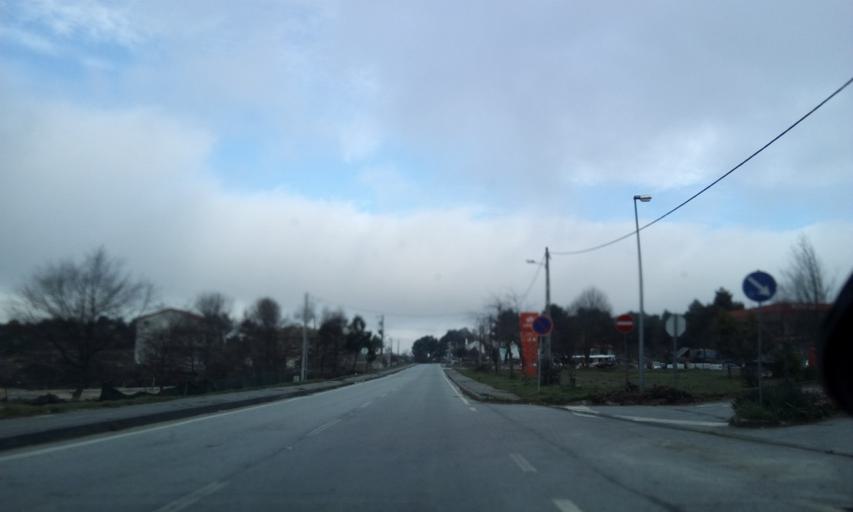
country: PT
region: Guarda
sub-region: Aguiar da Beira
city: Aguiar da Beira
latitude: 40.7414
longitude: -7.4964
